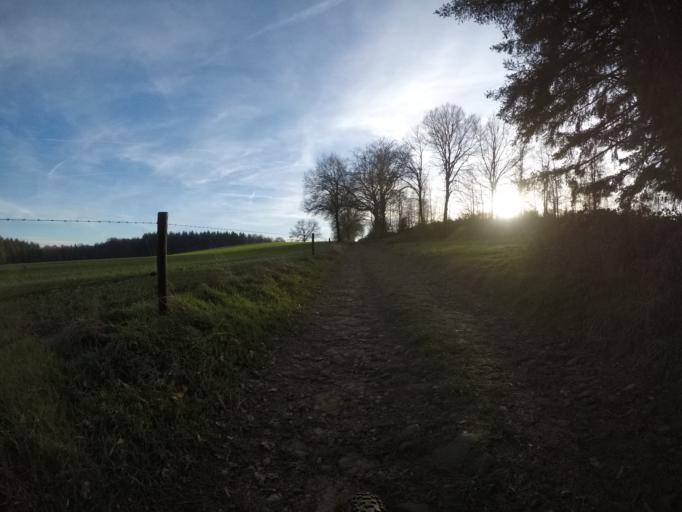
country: BE
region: Wallonia
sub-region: Province du Luxembourg
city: Tintigny
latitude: 49.6839
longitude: 5.4866
